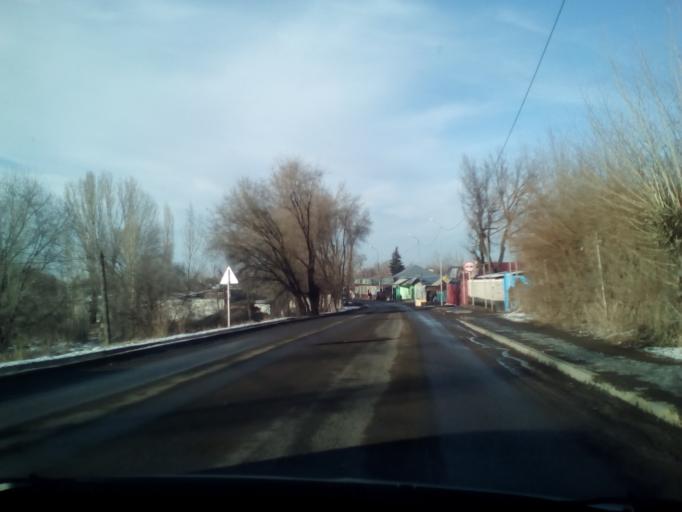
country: KZ
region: Almaty Oblysy
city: Burunday
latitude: 43.1604
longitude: 76.4166
